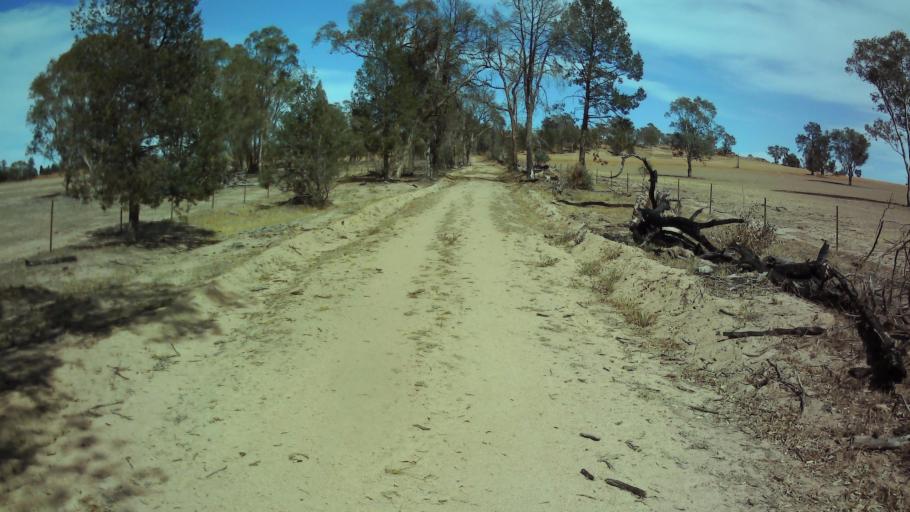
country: AU
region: New South Wales
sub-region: Weddin
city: Grenfell
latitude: -33.6802
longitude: 148.2673
